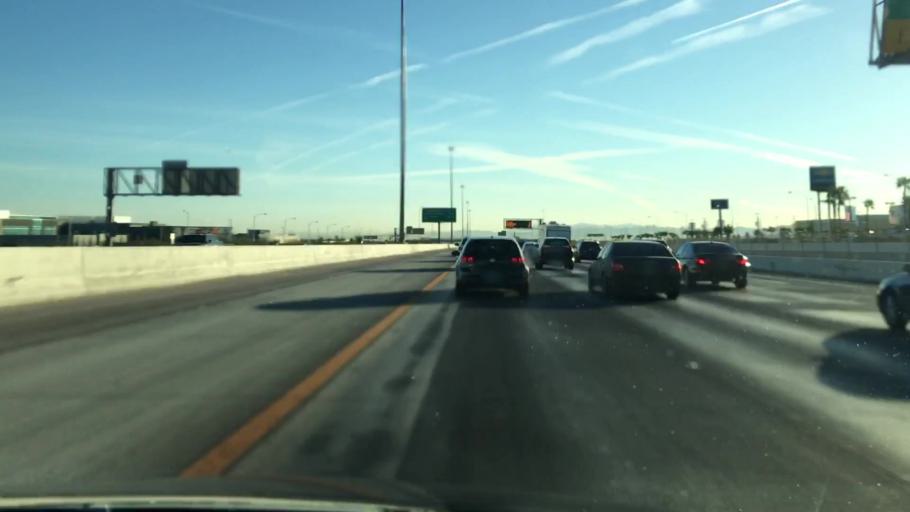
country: US
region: Nevada
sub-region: Clark County
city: Enterprise
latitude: 36.0667
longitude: -115.2356
